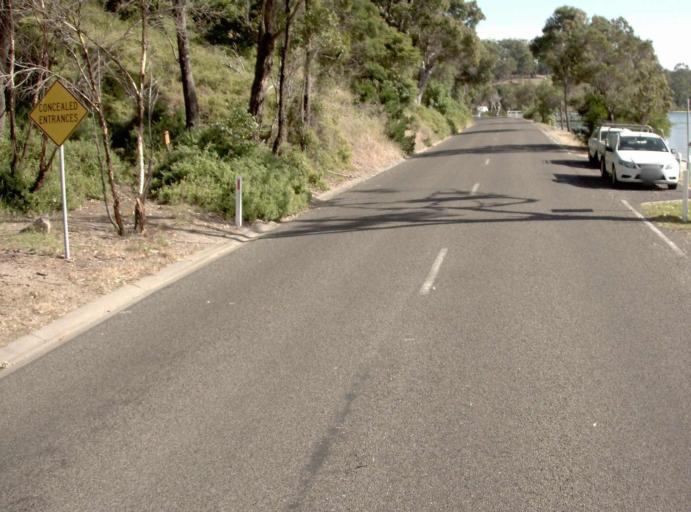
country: AU
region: Victoria
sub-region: East Gippsland
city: Lakes Entrance
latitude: -37.8848
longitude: 147.8598
